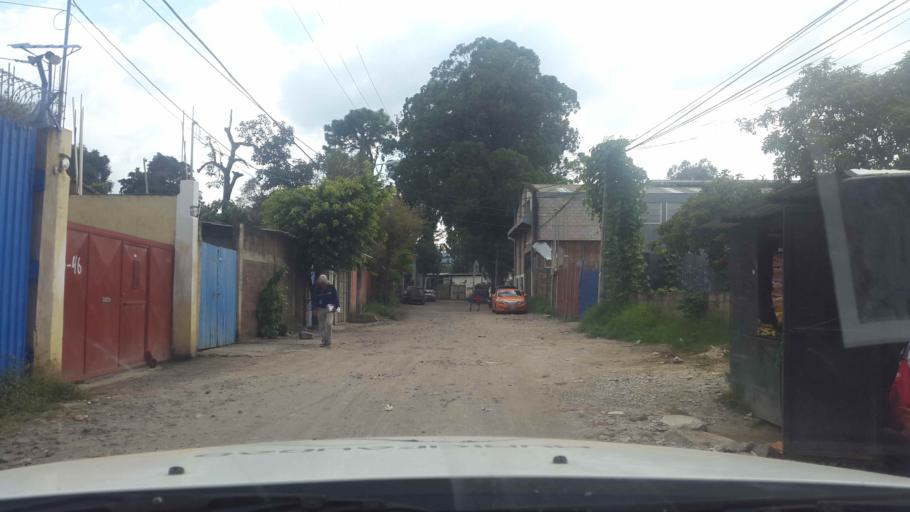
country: GT
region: Guatemala
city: Petapa
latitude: 14.5081
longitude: -90.5382
